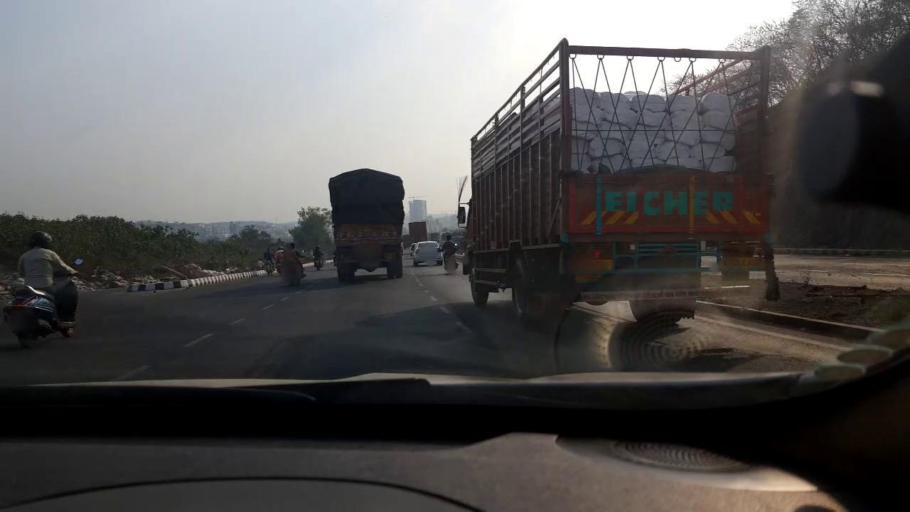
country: IN
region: Maharashtra
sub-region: Pune Division
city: Shivaji Nagar
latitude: 18.5374
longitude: 73.7814
